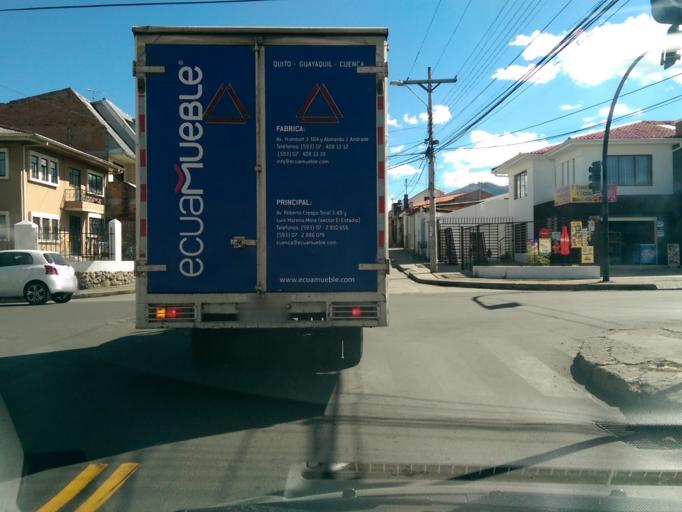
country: EC
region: Azuay
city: Cuenca
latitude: -2.9020
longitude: -79.0202
